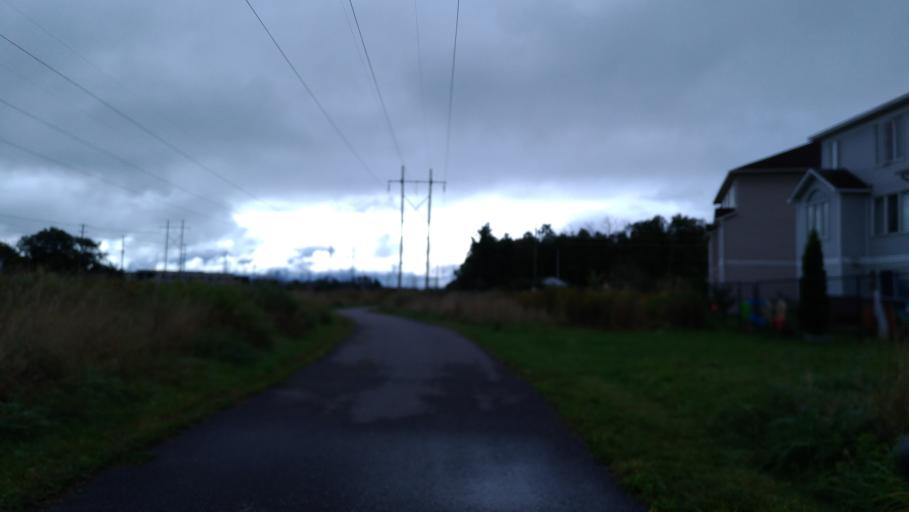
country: CA
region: Ontario
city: Bells Corners
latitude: 45.3439
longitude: -75.9361
